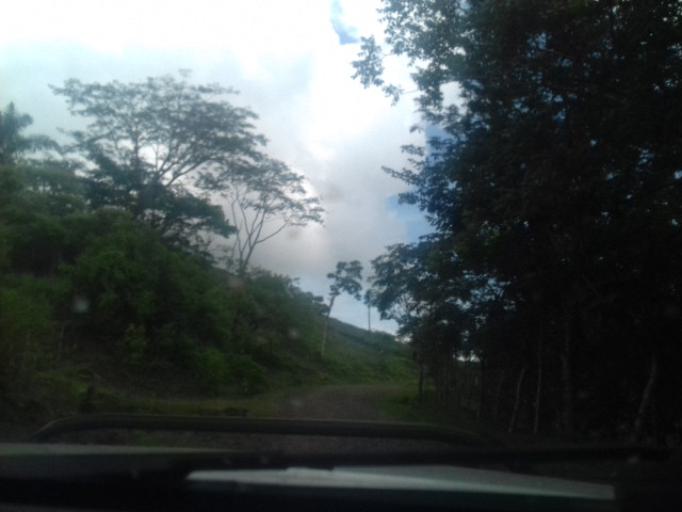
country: NI
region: Matagalpa
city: Matiguas
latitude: 12.9082
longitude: -85.3593
